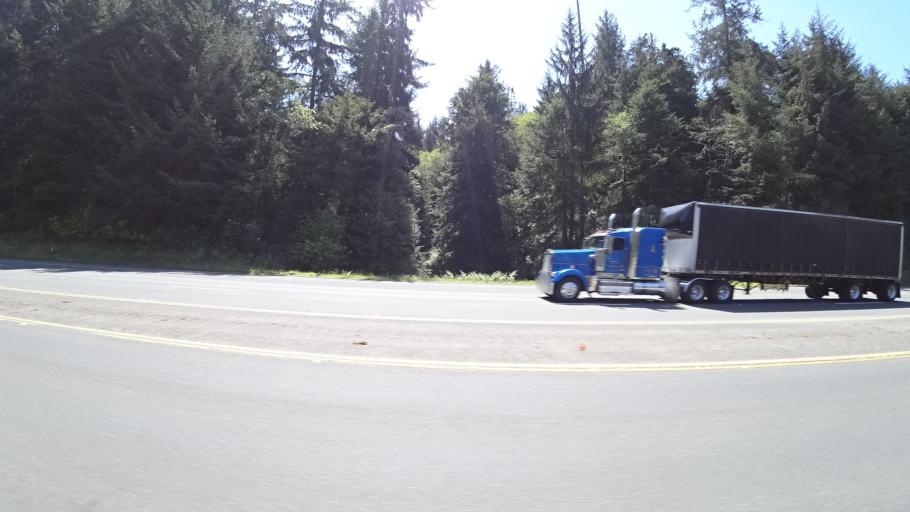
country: US
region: California
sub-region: Humboldt County
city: Westhaven-Moonstone
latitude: 41.1372
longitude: -124.1439
